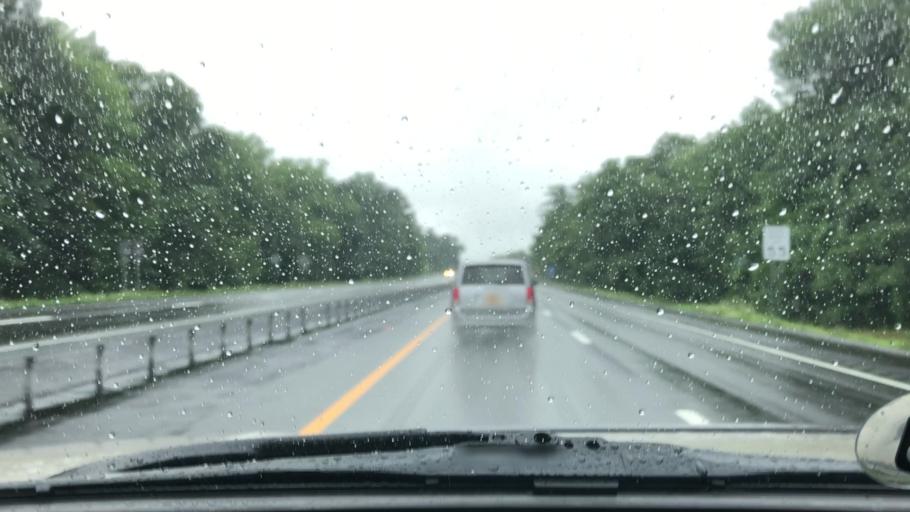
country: US
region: New York
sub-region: Greene County
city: Cairo
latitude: 42.2978
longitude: -73.9901
